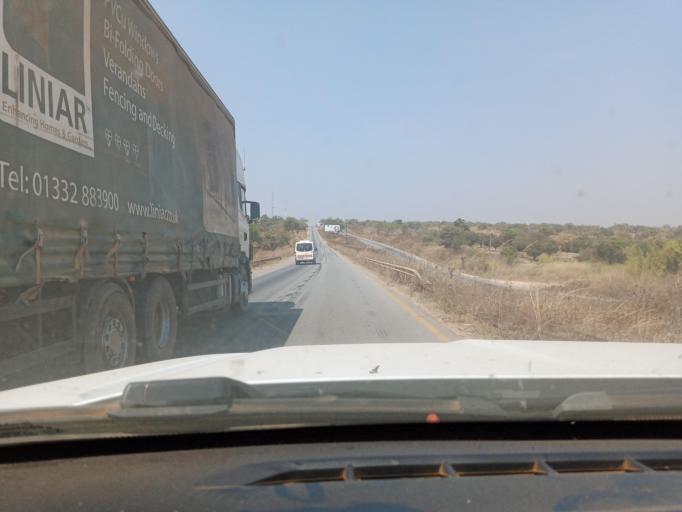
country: ZM
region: Copperbelt
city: Luanshya
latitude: -13.0167
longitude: 28.4365
